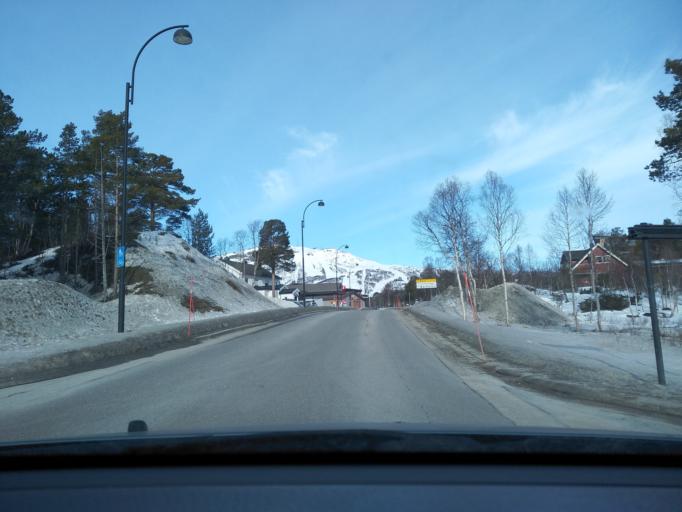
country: NO
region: Aust-Agder
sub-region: Bykle
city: Hovden
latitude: 59.5583
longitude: 7.3576
